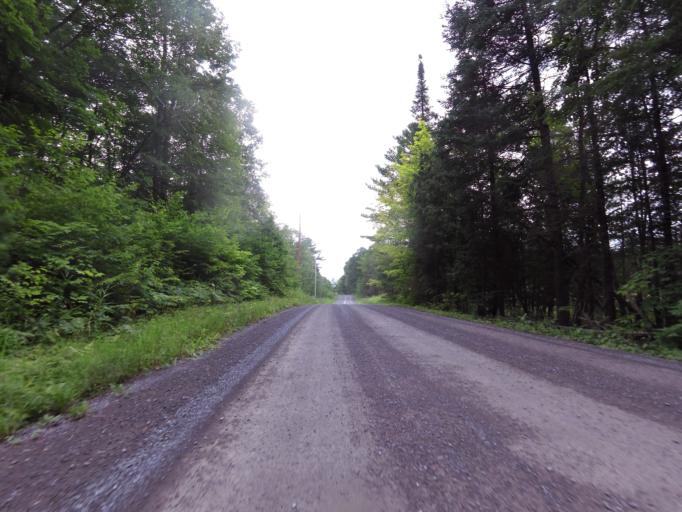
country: CA
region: Ontario
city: Carleton Place
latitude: 45.1551
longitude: -76.2622
